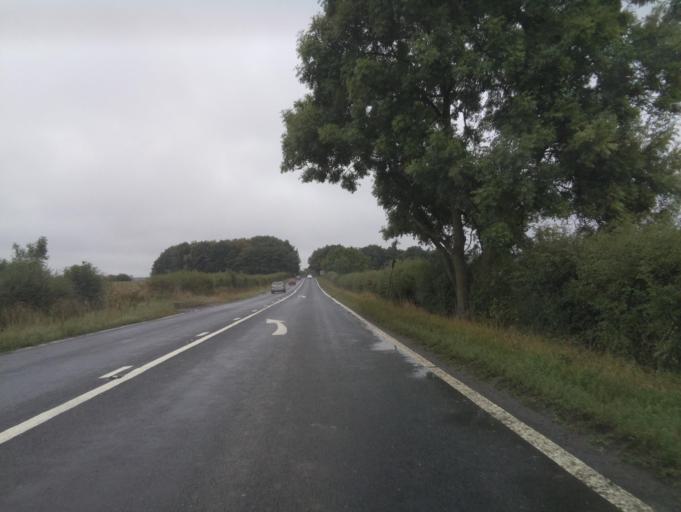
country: GB
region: England
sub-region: North Yorkshire
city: Pannal
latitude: 53.9276
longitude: -1.5351
